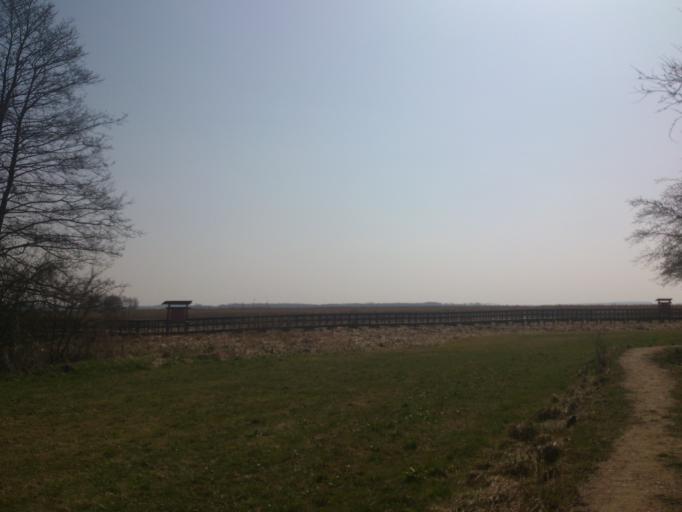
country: PL
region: Podlasie
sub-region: Powiat bialostocki
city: Tykocin
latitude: 53.1060
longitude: 22.7974
